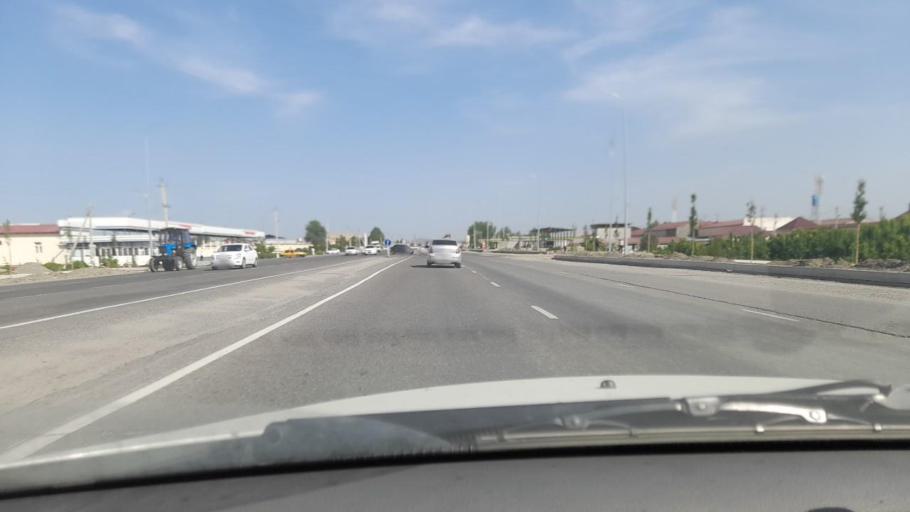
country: UZ
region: Samarqand
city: Daxbet
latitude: 39.7295
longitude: 66.9407
